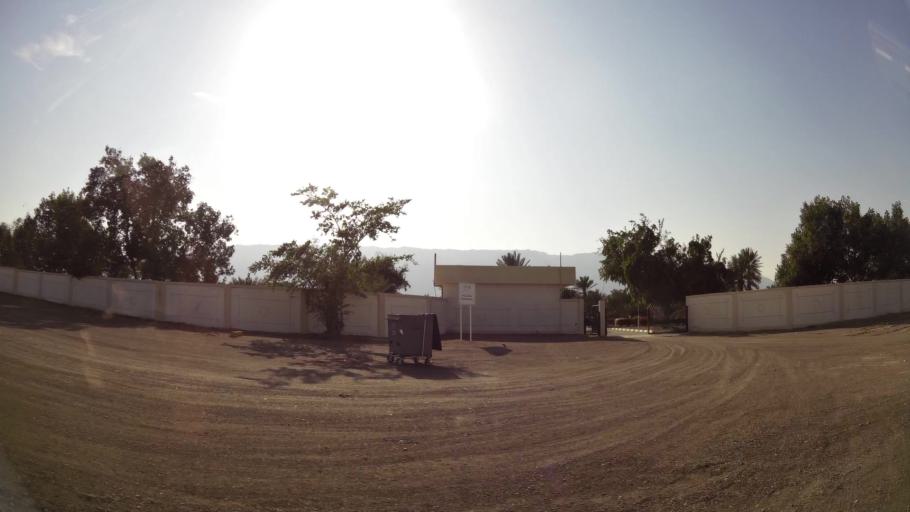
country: AE
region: Abu Dhabi
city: Al Ain
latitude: 24.0529
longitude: 55.8403
